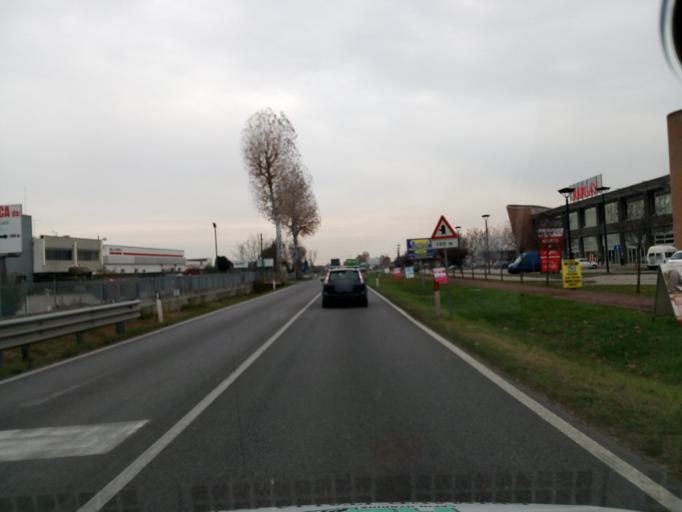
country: IT
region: Veneto
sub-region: Provincia di Treviso
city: Falze-Signoressa
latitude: 45.7553
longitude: 12.0978
